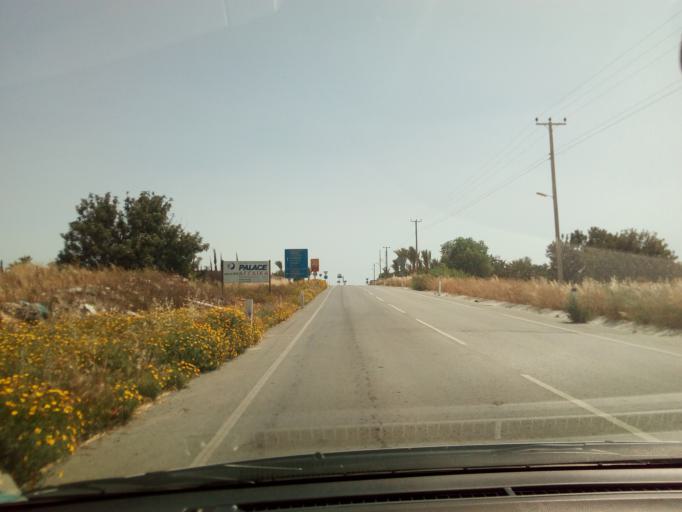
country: CY
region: Larnaka
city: Athienou
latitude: 35.0512
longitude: 33.5405
